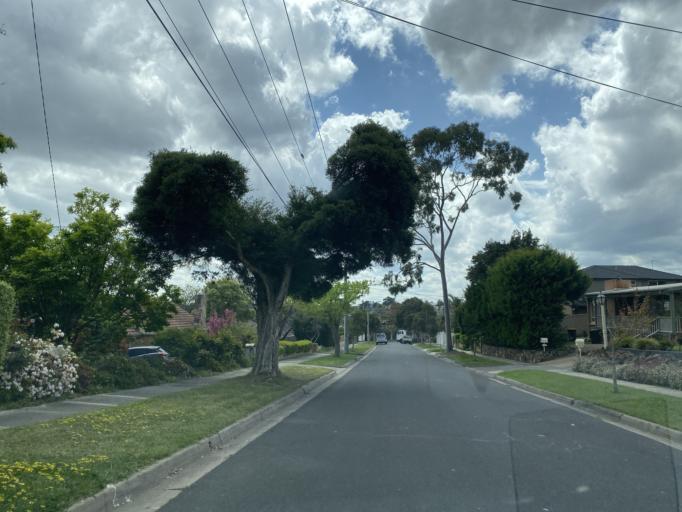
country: AU
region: Victoria
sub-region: Whitehorse
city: Burwood
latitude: -37.8582
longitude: 145.1243
